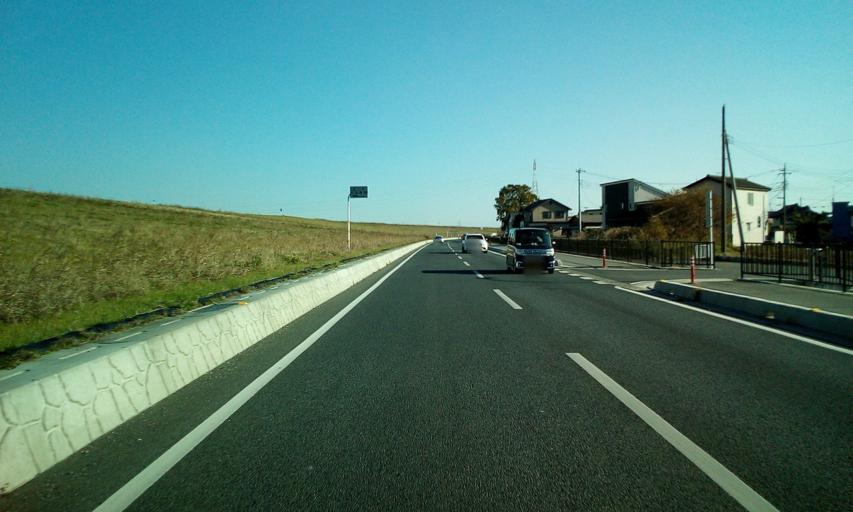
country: JP
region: Chiba
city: Noda
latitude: 35.9310
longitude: 139.8551
